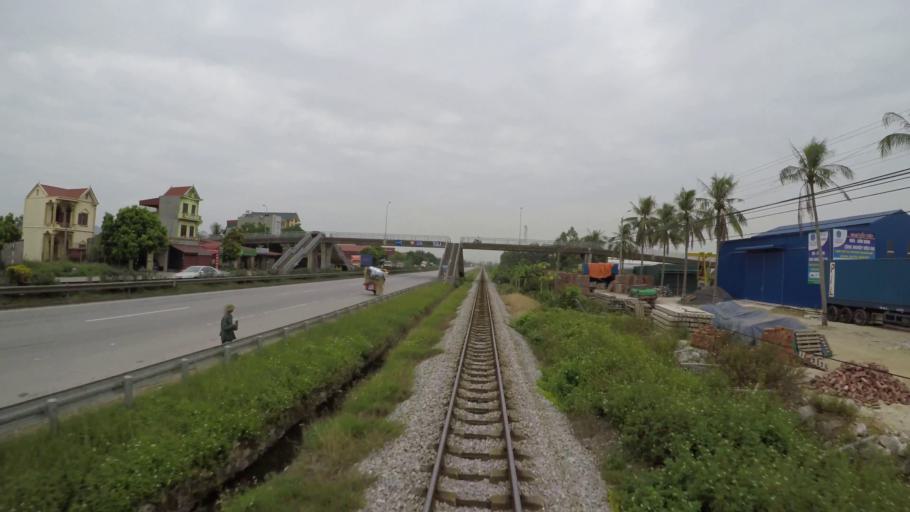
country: VN
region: Hai Duong
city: Phu Thai
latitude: 20.9689
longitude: 106.4498
